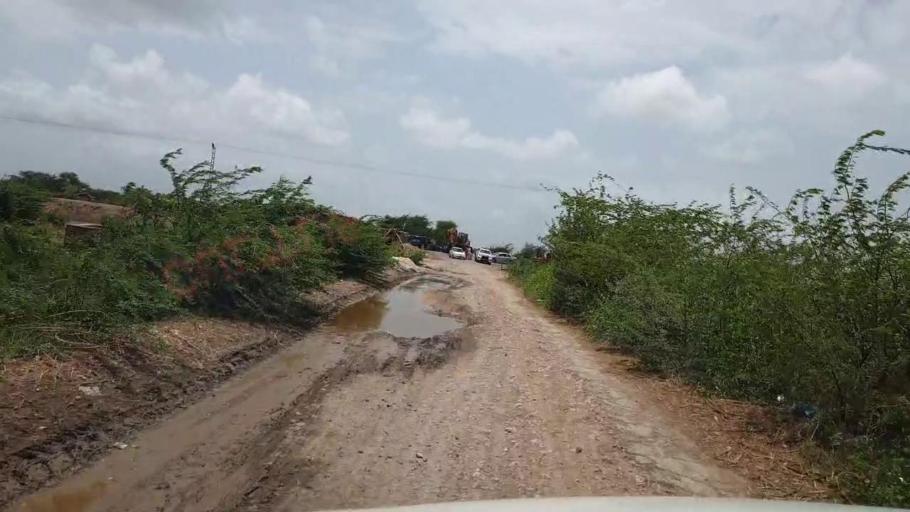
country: PK
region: Sindh
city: Kario
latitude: 24.7242
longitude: 68.5625
